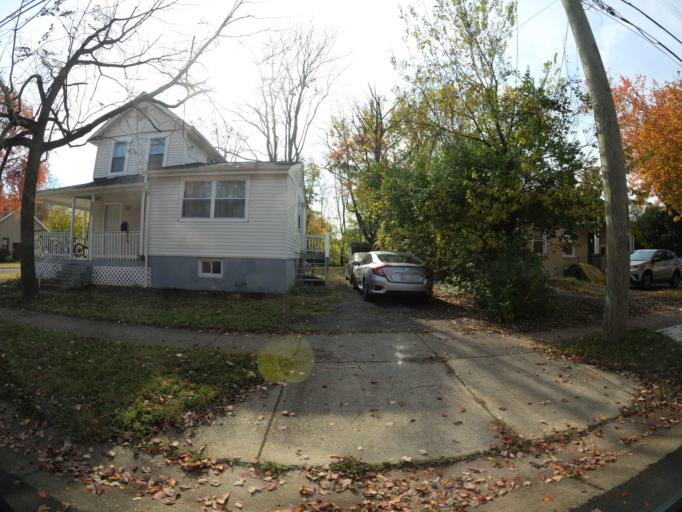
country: US
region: Maryland
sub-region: Prince George's County
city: College Park
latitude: 38.9887
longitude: -76.9267
